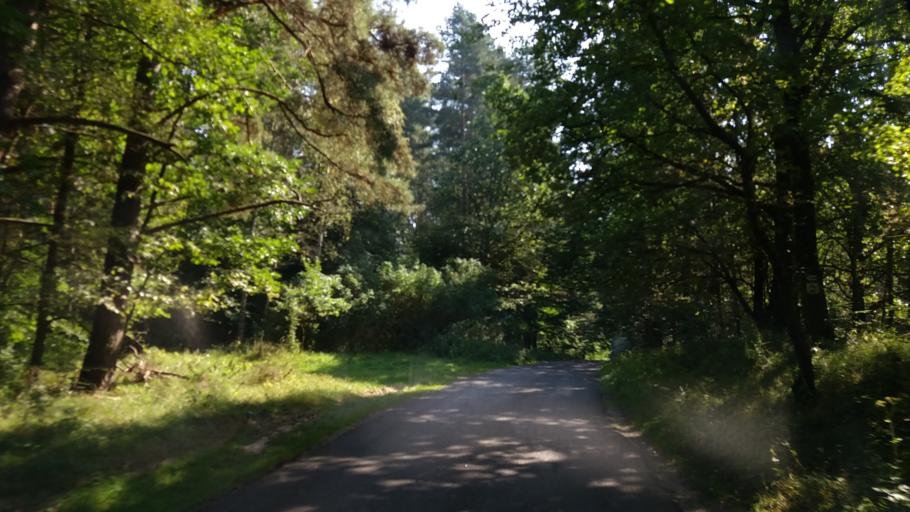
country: PL
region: West Pomeranian Voivodeship
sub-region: Powiat walecki
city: Czlopa
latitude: 53.0775
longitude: 15.9273
